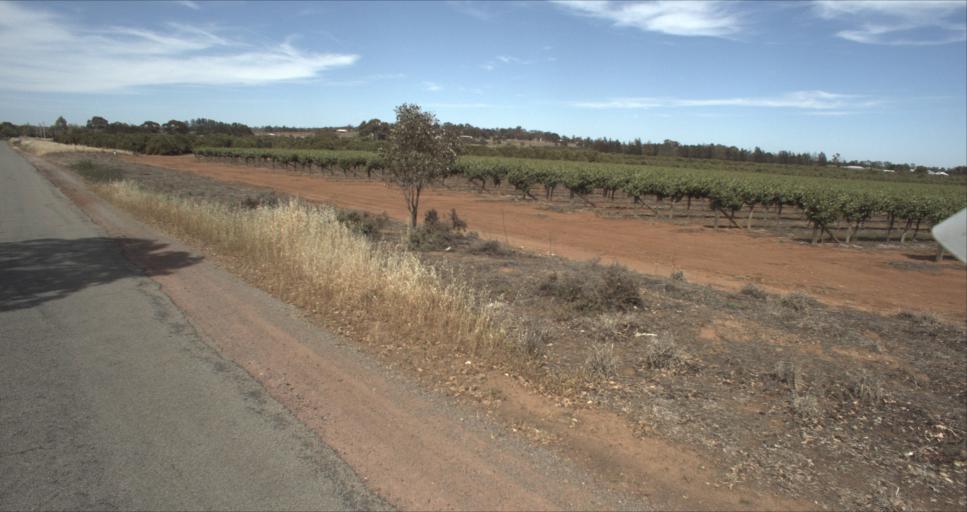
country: AU
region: New South Wales
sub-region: Leeton
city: Leeton
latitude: -34.5671
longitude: 146.4561
